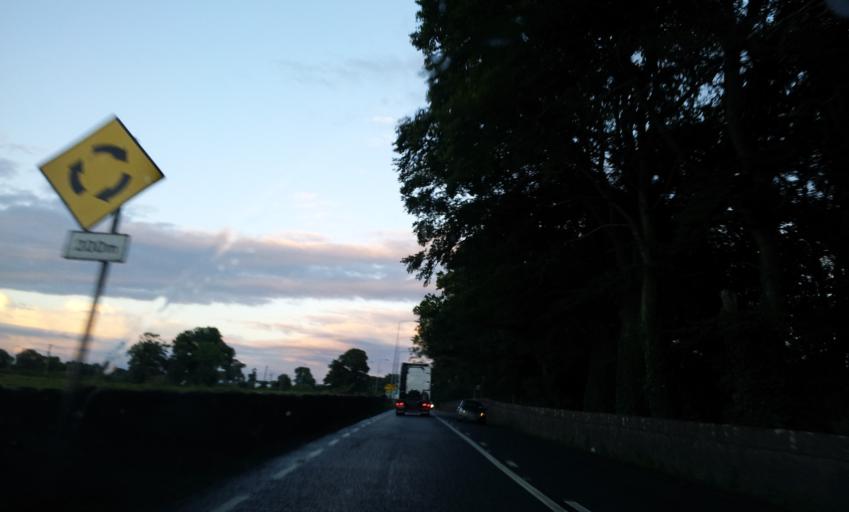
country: IE
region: Munster
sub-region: County Limerick
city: Adare
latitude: 52.5734
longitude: -8.7773
